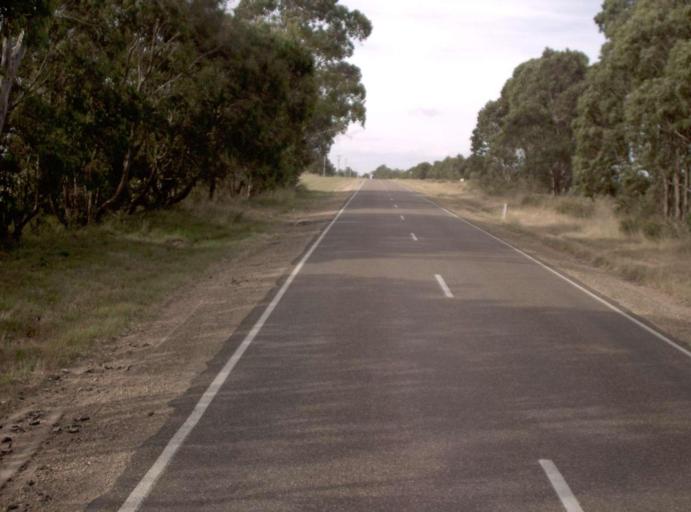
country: AU
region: Victoria
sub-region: Wellington
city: Heyfield
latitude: -38.0431
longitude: 146.6653
